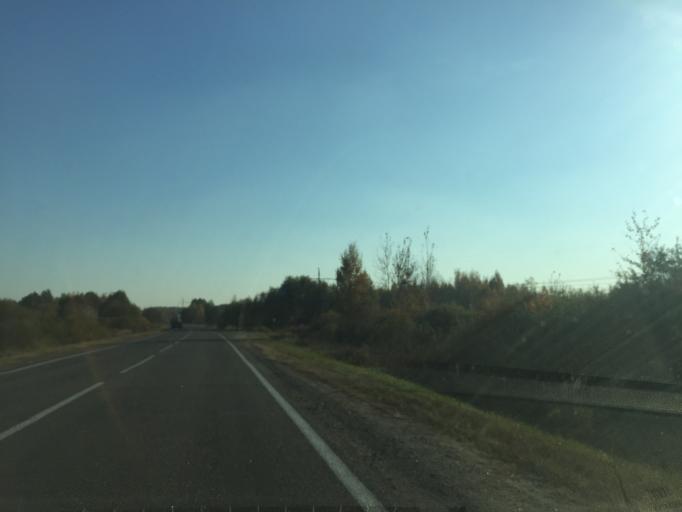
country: BY
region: Gomel
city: Dobrush
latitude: 52.3456
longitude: 31.2300
